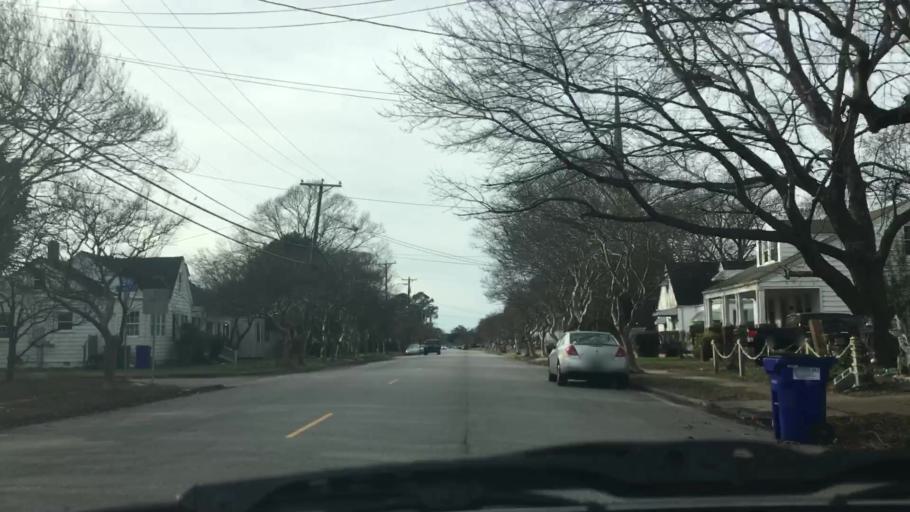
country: US
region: Virginia
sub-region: City of Norfolk
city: Norfolk
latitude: 36.8899
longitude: -76.2413
